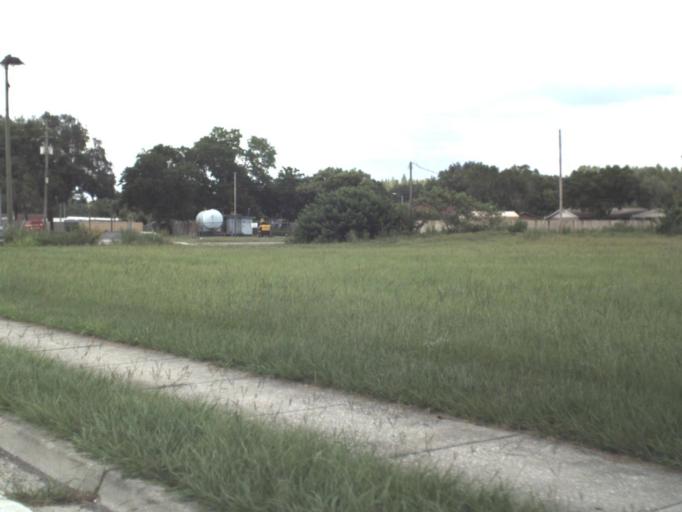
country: US
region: Florida
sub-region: Hillsborough County
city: Lutz
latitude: 28.1711
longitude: -82.4609
